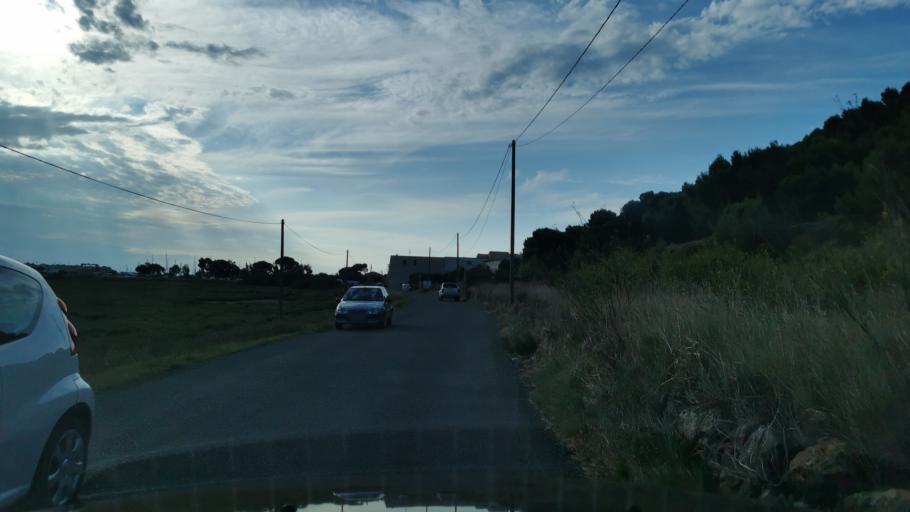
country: FR
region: Languedoc-Roussillon
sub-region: Departement de l'Aude
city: Gruissan
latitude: 43.1053
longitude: 3.0807
